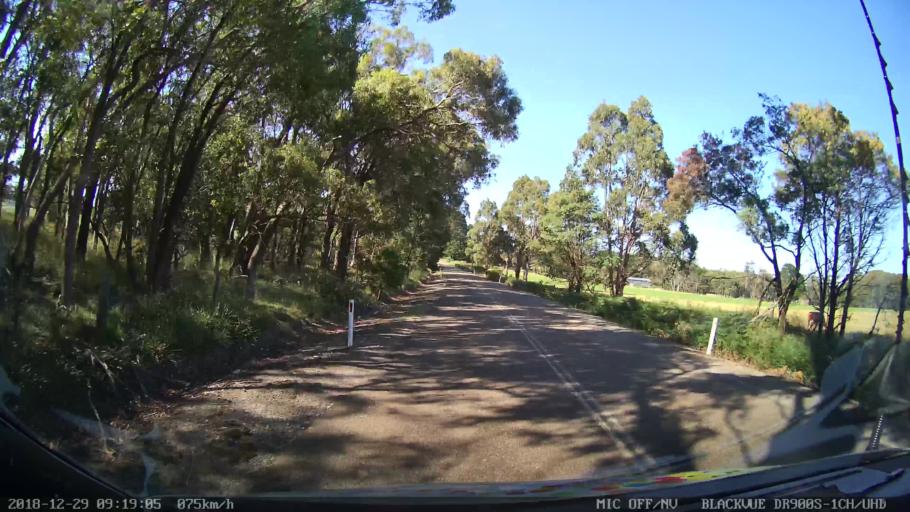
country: AU
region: New South Wales
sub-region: Upper Lachlan Shire
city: Crookwell
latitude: -34.4776
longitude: 149.4307
